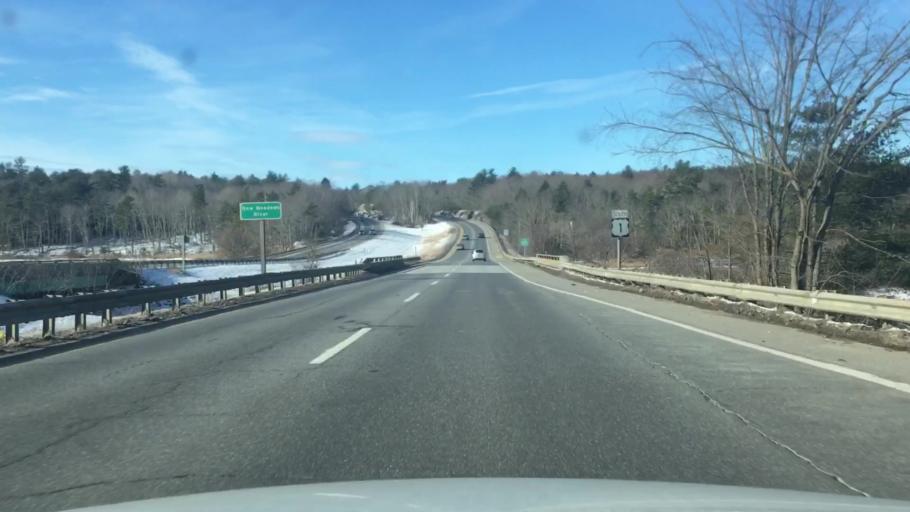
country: US
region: Maine
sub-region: Sagadahoc County
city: Bath
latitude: 43.9182
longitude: -69.8644
